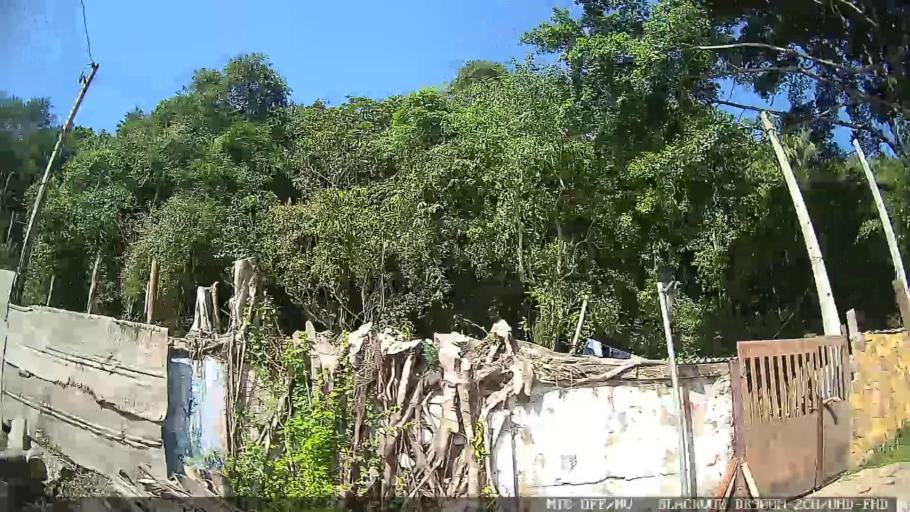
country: BR
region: Sao Paulo
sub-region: Guaruja
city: Guaruja
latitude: -24.0079
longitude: -46.2869
